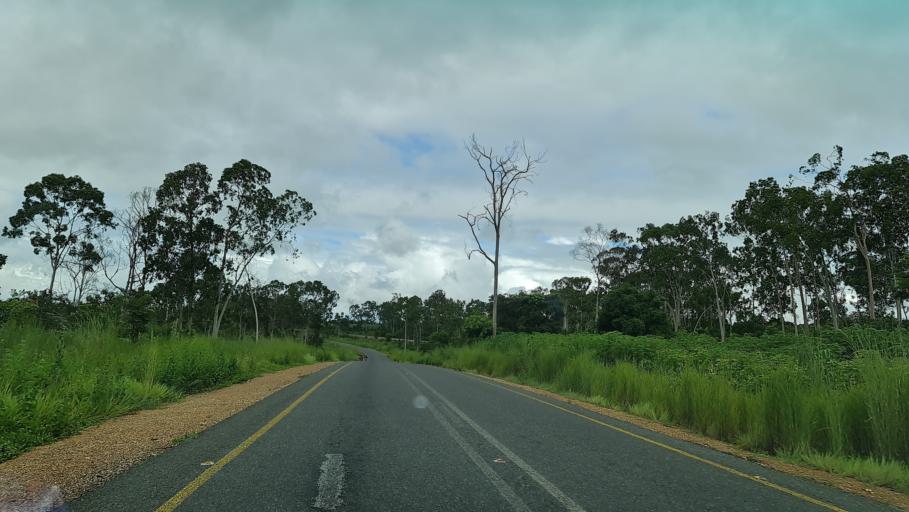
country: MZ
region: Nampula
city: Nampula
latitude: -14.9818
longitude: 38.5216
